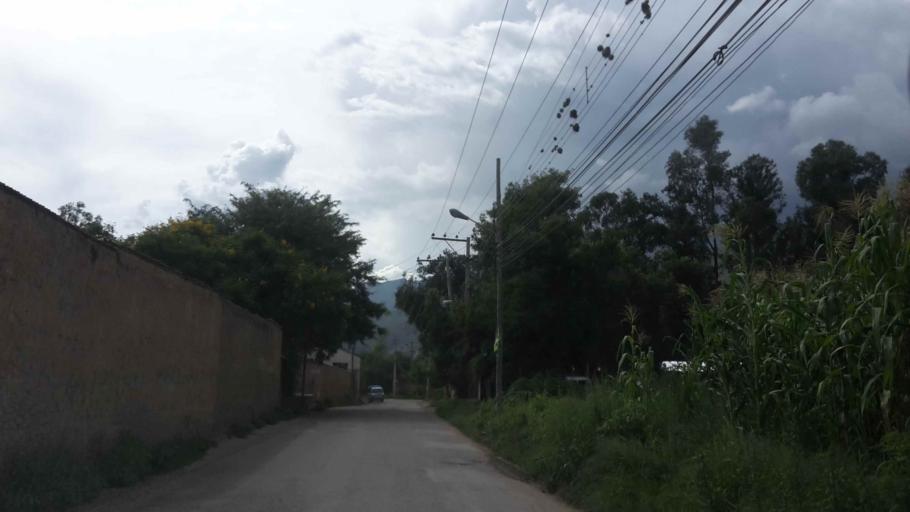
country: BO
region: Cochabamba
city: Cochabamba
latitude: -17.3325
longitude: -66.2376
